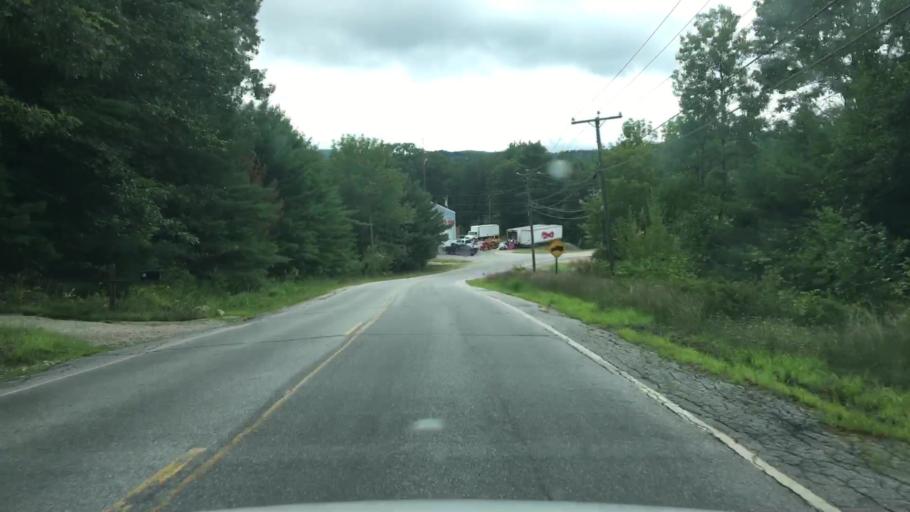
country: US
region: Maine
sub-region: York County
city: Cornish
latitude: 43.8093
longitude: -70.7783
